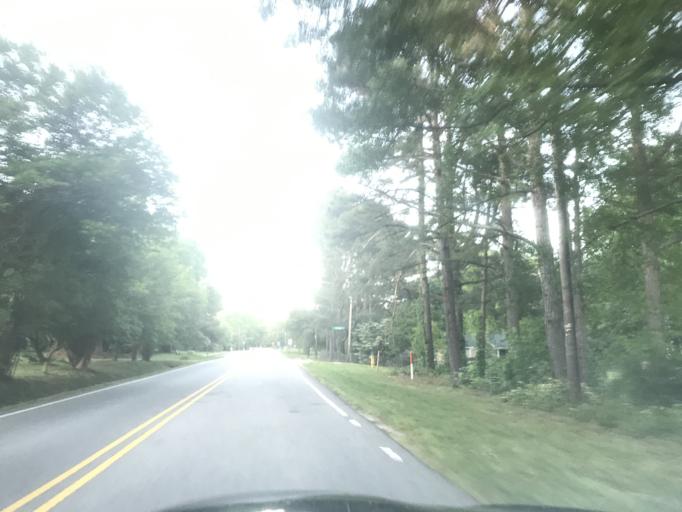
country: US
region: North Carolina
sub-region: Wake County
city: Wendell
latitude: 35.7777
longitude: -78.3772
